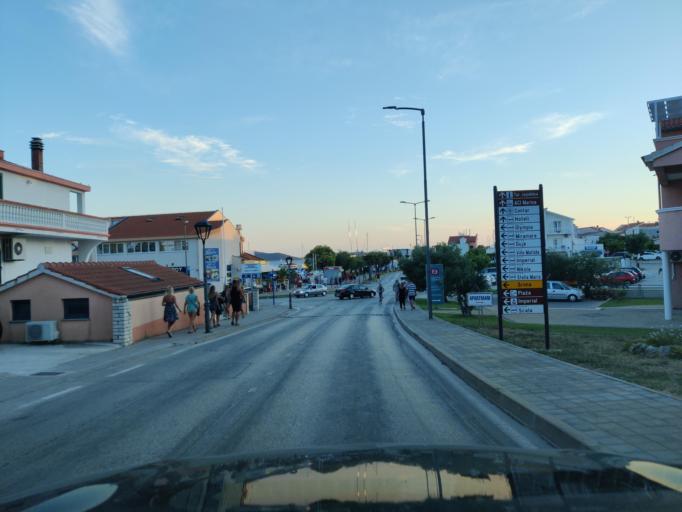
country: HR
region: Sibensko-Kniniska
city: Vodice
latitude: 43.7591
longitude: 15.7824
